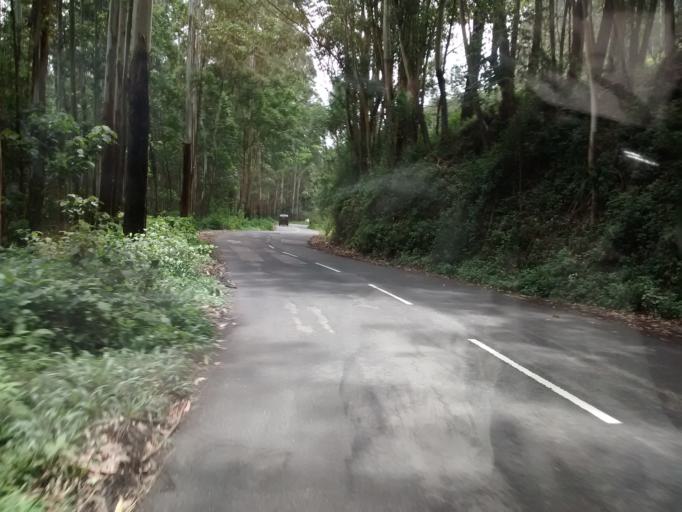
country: IN
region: Kerala
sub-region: Idukki
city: Munnar
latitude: 10.1186
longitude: 77.1421
